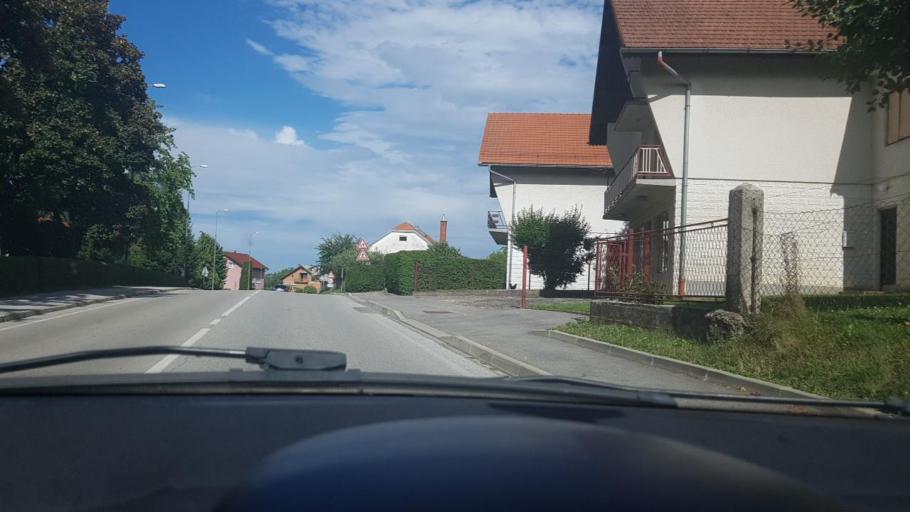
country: HR
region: Varazdinska
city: Lepoglava
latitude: 46.2075
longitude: 16.0445
